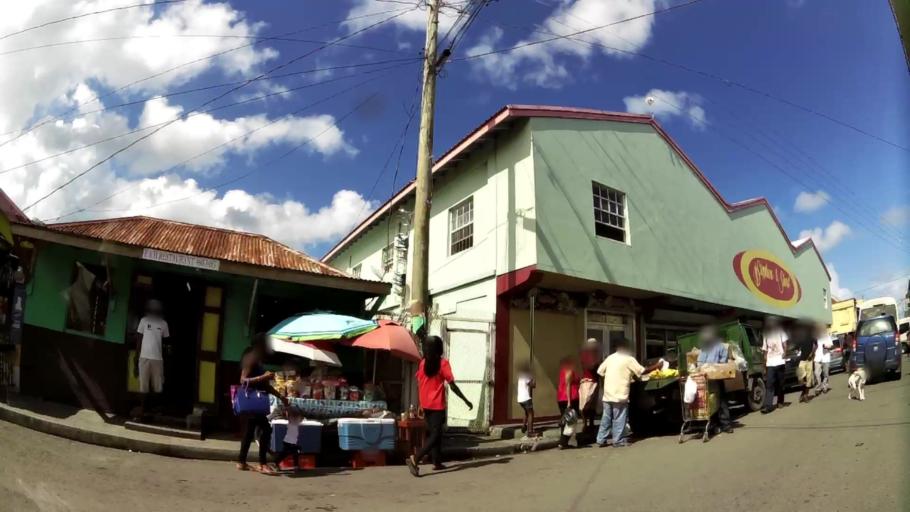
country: AG
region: Saint John
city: Saint John's
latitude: 17.1189
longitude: -61.8437
